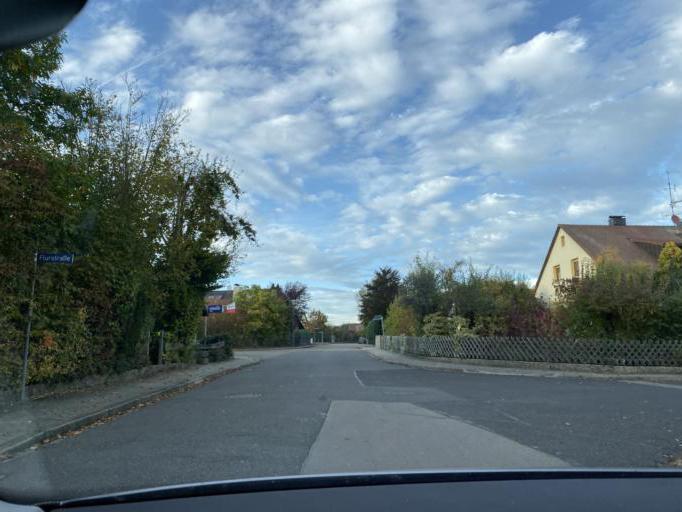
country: DE
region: Bavaria
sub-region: Regierungsbezirk Mittelfranken
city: Puschendorf
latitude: 49.5248
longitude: 10.8357
